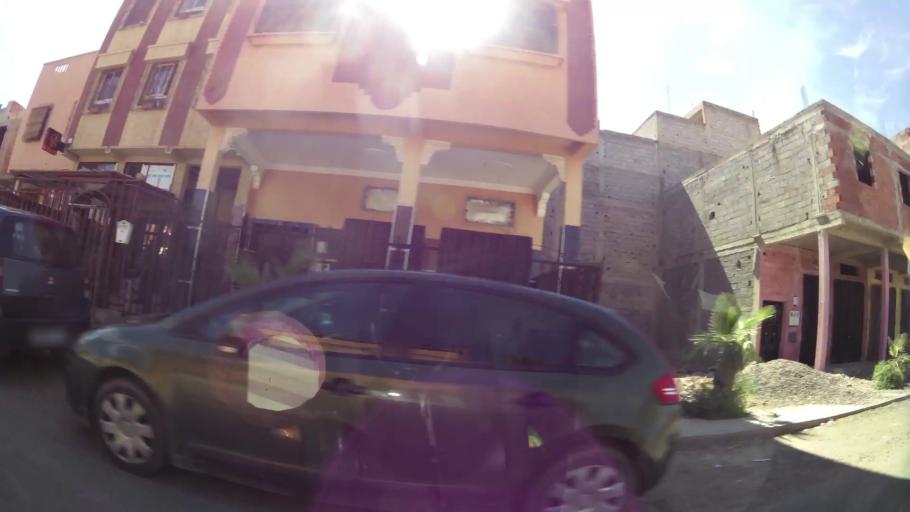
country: MA
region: Marrakech-Tensift-Al Haouz
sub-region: Marrakech
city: Marrakesh
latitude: 31.6391
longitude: -8.1071
